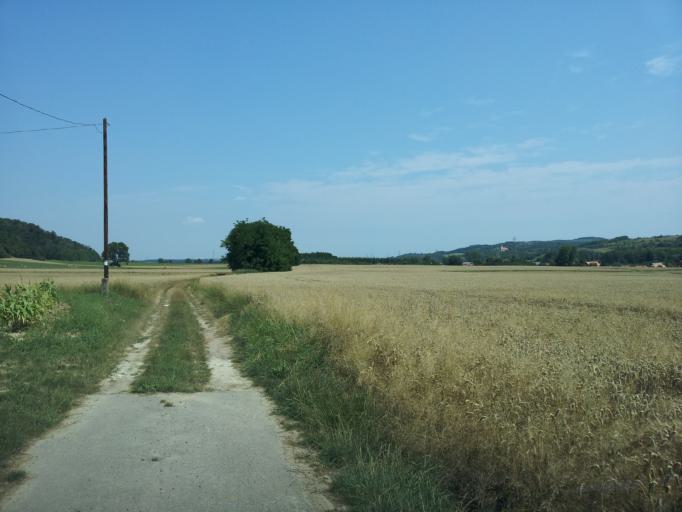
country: HU
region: Zala
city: Zalaegerszeg
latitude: 46.8525
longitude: 16.9289
